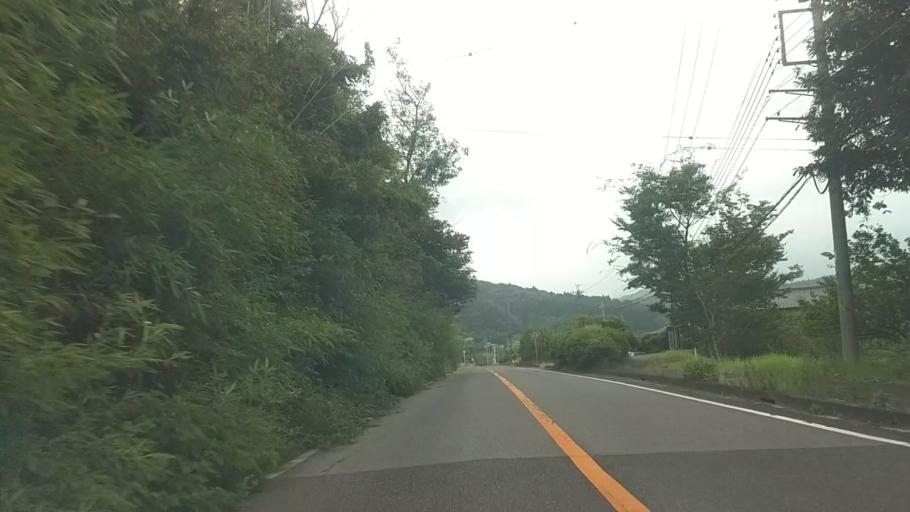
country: JP
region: Chiba
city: Kimitsu
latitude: 35.2195
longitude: 139.9450
